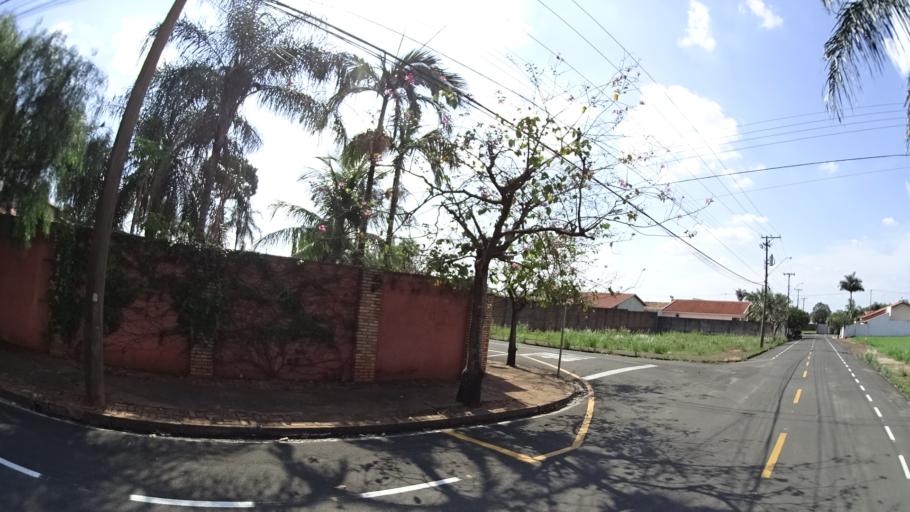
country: BR
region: Sao Paulo
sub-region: Sao Jose Do Rio Preto
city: Sao Jose do Rio Preto
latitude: -20.8557
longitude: -49.4088
